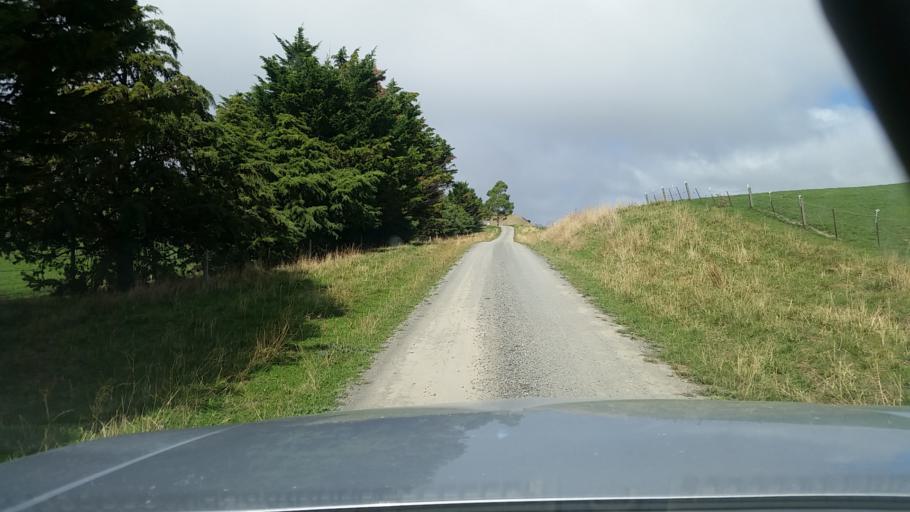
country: NZ
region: Marlborough
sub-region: Marlborough District
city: Blenheim
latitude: -41.7511
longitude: 173.8965
